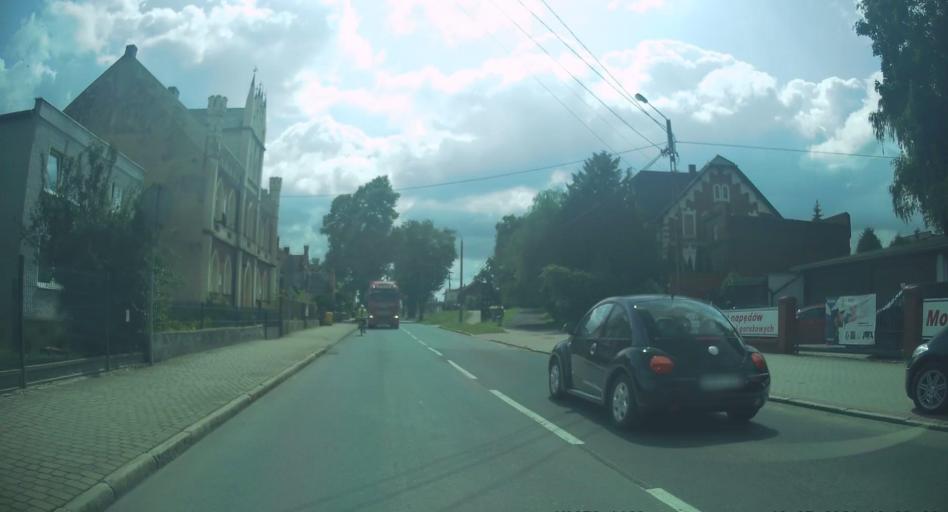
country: PL
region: Opole Voivodeship
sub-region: Powiat prudnicki
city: Glogowek
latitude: 50.3528
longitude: 17.8681
